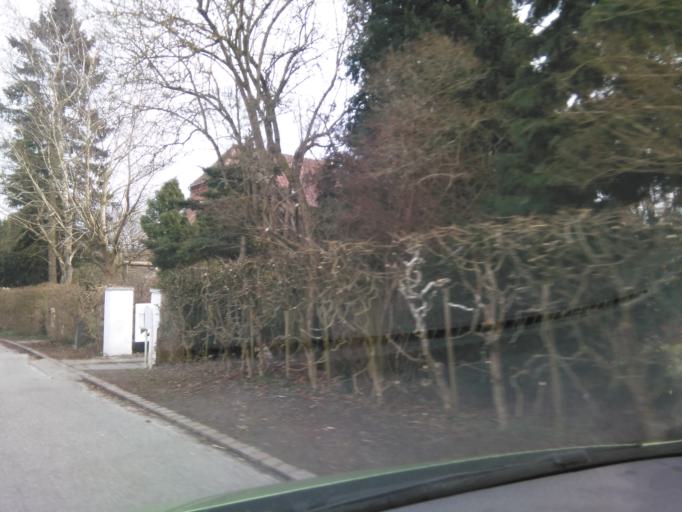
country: DK
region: Central Jutland
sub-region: Arhus Kommune
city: Arhus
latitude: 56.1175
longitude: 10.2040
